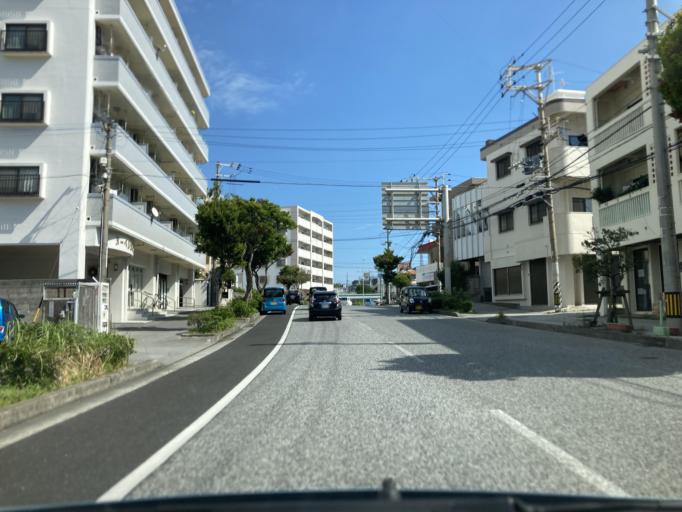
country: JP
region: Okinawa
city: Ginowan
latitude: 26.2547
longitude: 127.7554
